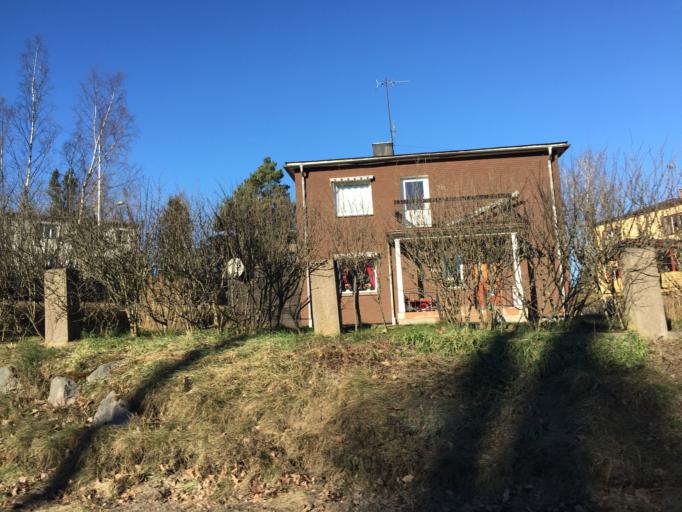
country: SE
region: OEstergoetland
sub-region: Finspangs Kommun
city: Finspang
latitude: 58.7100
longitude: 15.7503
